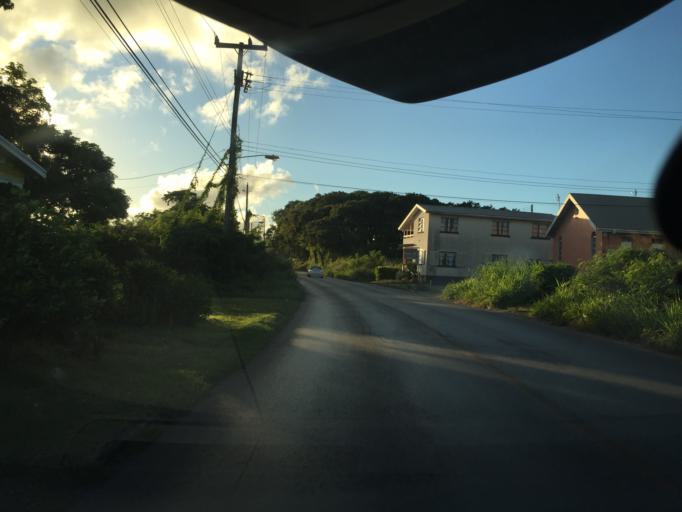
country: BB
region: Christ Church
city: Oistins
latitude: 13.0788
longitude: -59.5097
